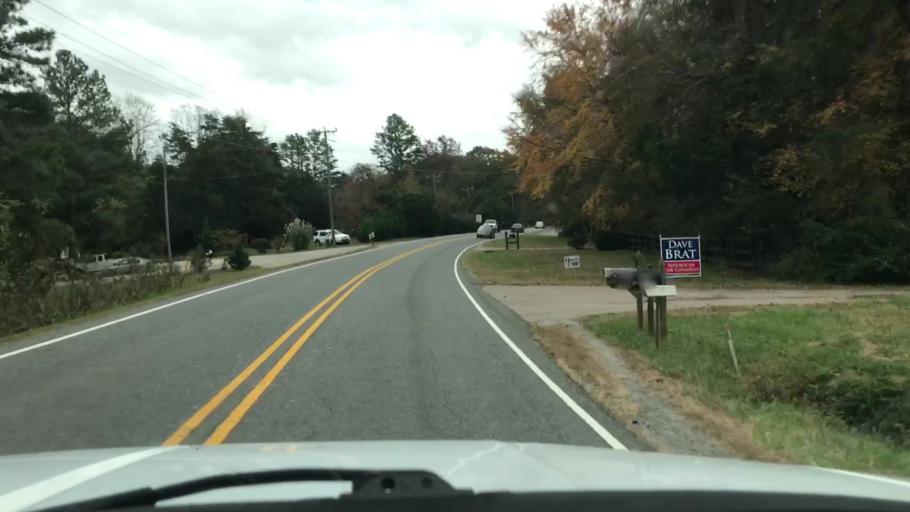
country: US
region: Virginia
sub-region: Goochland County
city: Goochland
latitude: 37.6353
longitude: -77.7912
